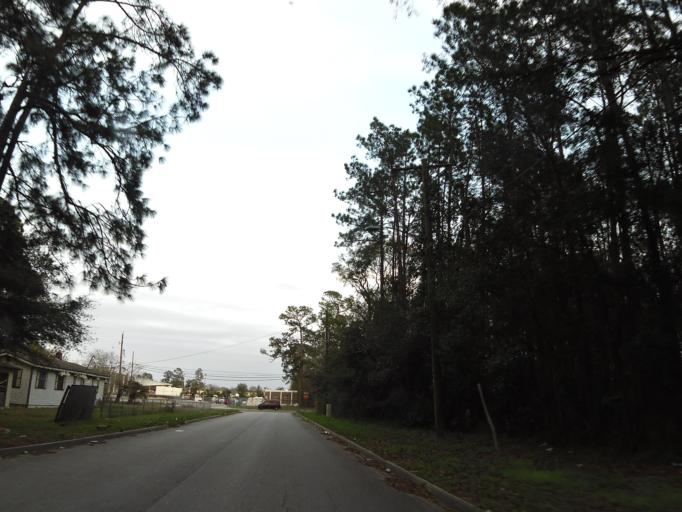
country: US
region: Florida
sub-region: Duval County
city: Jacksonville
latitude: 30.3580
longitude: -81.6982
